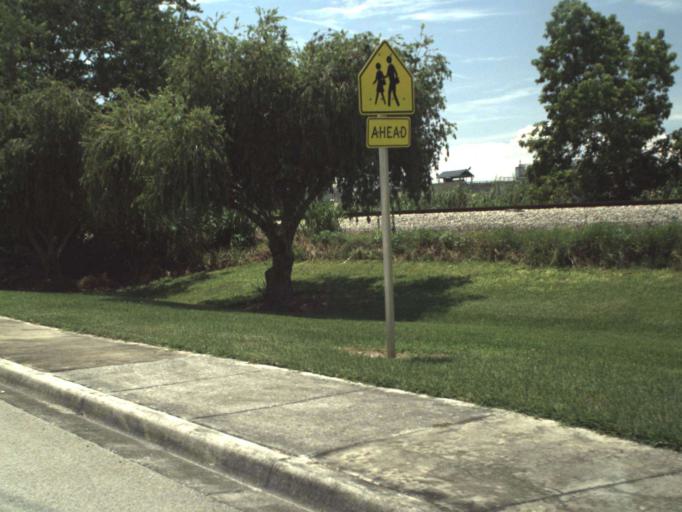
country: US
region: Florida
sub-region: Palm Beach County
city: Pahokee
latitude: 26.8641
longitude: -80.6312
